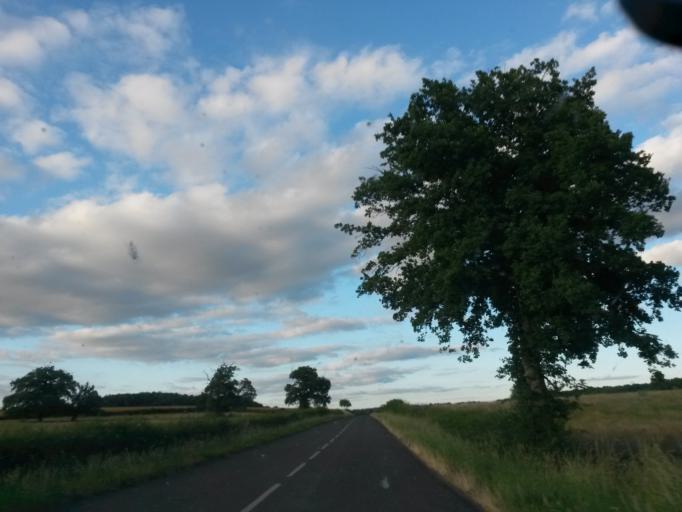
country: FR
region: Bourgogne
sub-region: Departement de la Nievre
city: Corbigny
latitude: 47.2284
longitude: 3.5466
